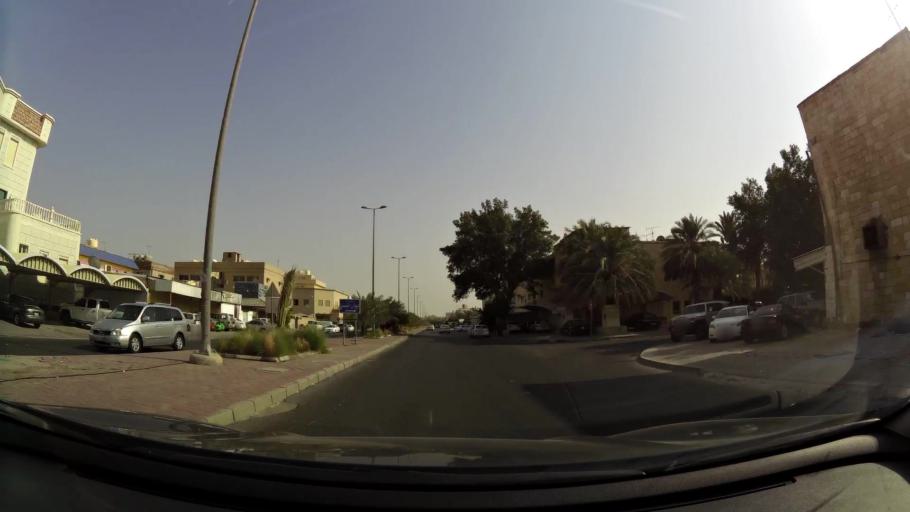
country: KW
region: Muhafazat al Jahra'
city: Al Jahra'
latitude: 29.3534
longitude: 47.6785
